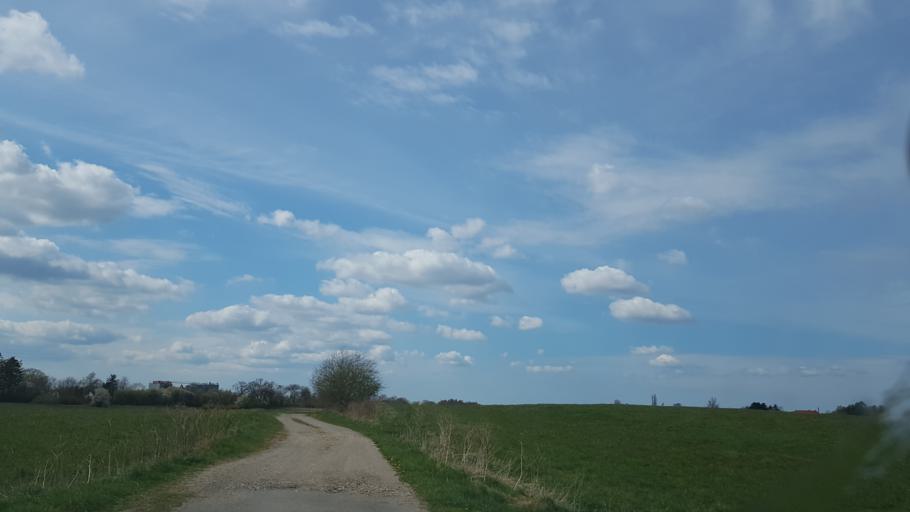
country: DK
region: Capital Region
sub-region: Allerod Kommune
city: Lillerod
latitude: 55.8936
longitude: 12.3398
